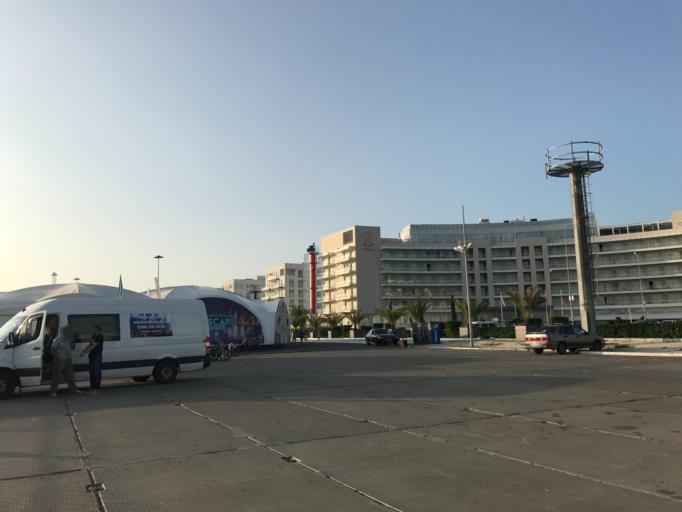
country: RU
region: Krasnodarskiy
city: Adler
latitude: 43.4100
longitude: 39.9360
